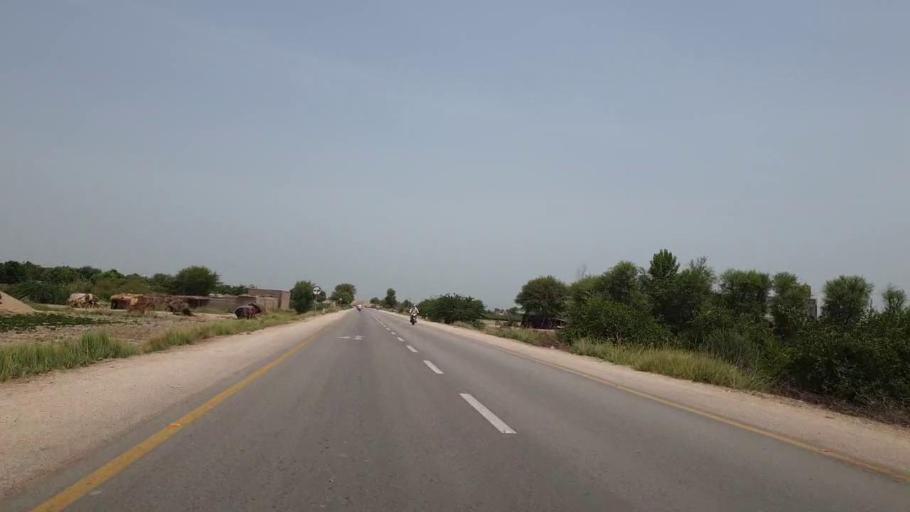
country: PK
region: Sindh
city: Shahpur Chakar
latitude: 26.1595
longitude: 68.6316
